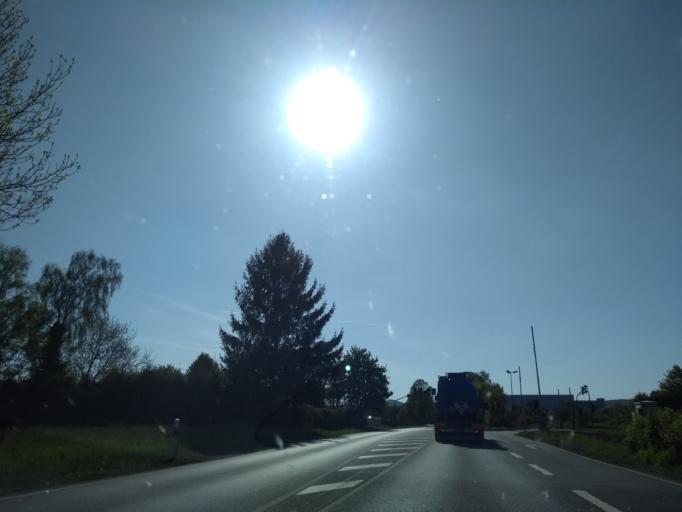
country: DE
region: Hesse
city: Allendorf
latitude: 51.0284
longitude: 8.6979
